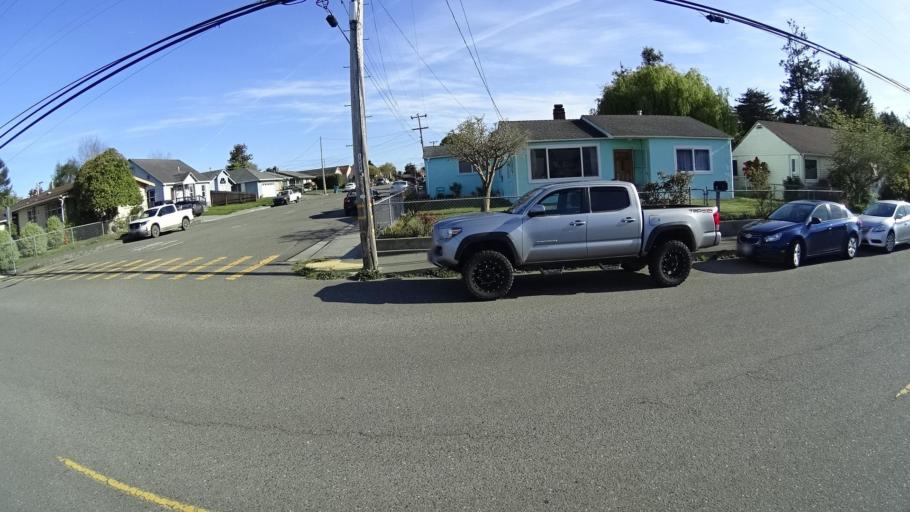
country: US
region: California
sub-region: Humboldt County
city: Cutten
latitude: 40.7711
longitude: -124.1625
